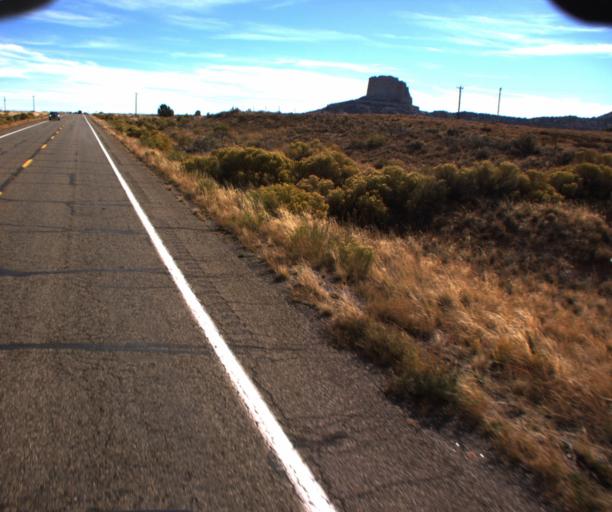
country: US
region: Arizona
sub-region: Coconino County
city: Kaibito
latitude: 36.6166
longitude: -110.9501
